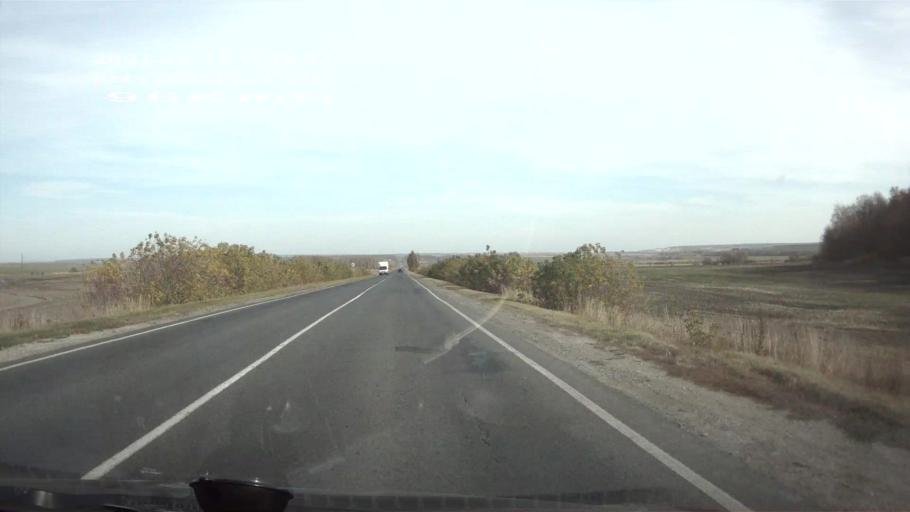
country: RU
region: Mordoviya
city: Atyashevo
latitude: 54.5381
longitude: 45.9300
